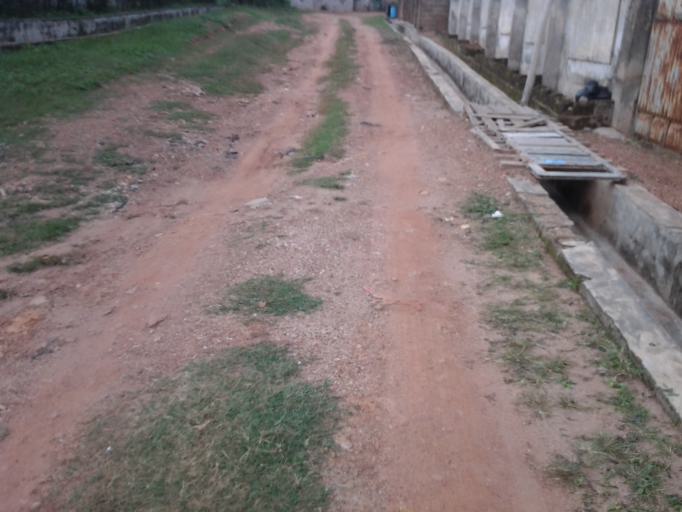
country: NG
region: Oyo
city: Ibadan
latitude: 7.4350
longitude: 3.9470
